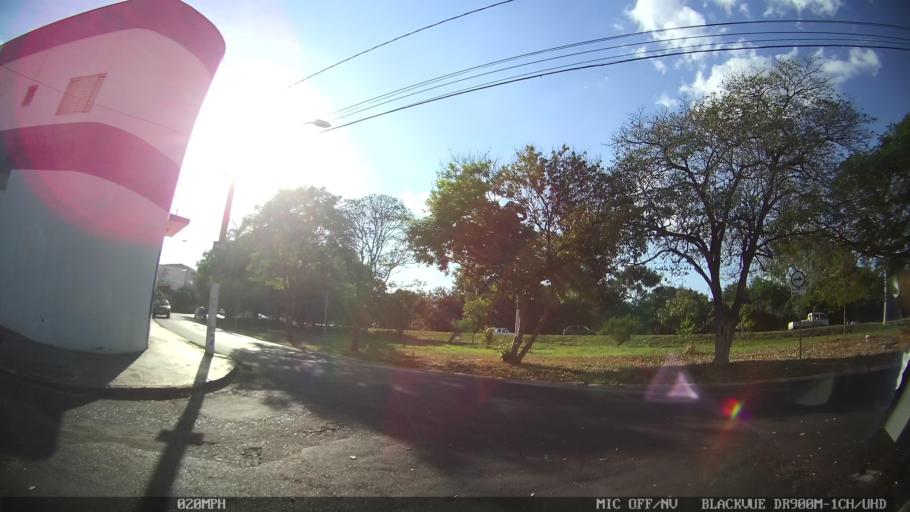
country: BR
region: Sao Paulo
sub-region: Ribeirao Preto
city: Ribeirao Preto
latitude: -21.1881
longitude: -47.7855
